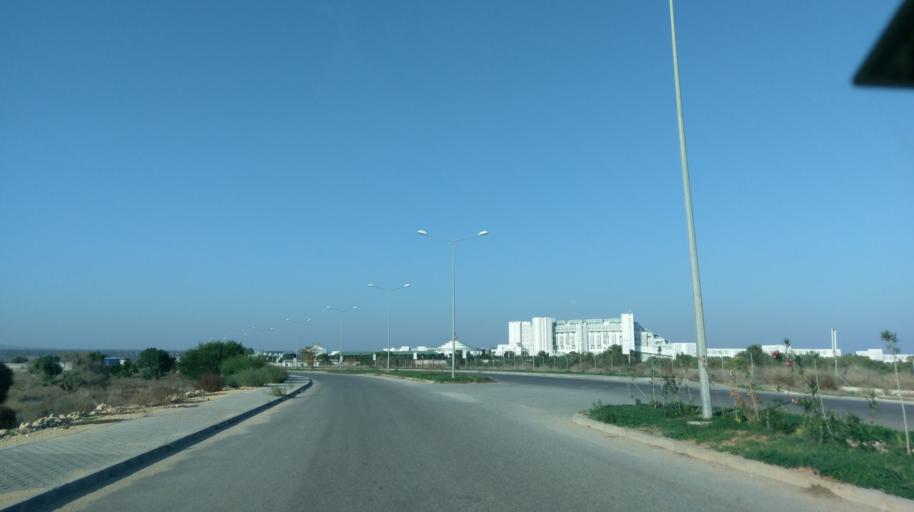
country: CY
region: Ammochostos
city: Leonarisso
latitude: 35.3592
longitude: 34.0711
